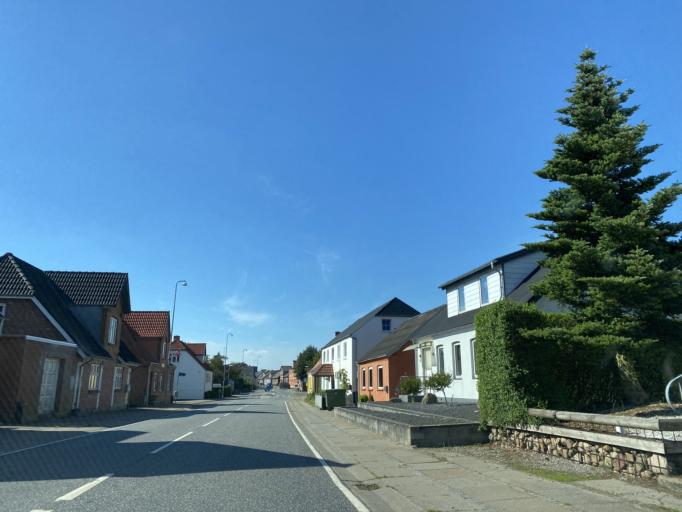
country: DK
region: Central Jutland
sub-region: Hedensted Kommune
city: Torring
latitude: 55.8602
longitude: 9.4182
